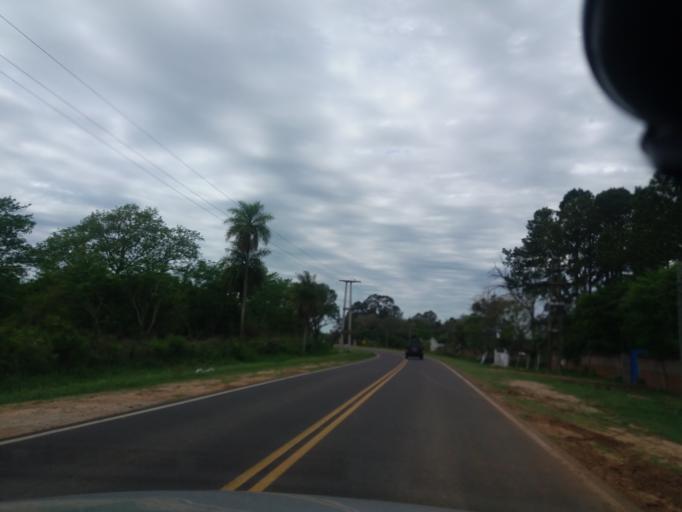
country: AR
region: Corrientes
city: Corrientes
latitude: -27.4558
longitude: -58.7181
